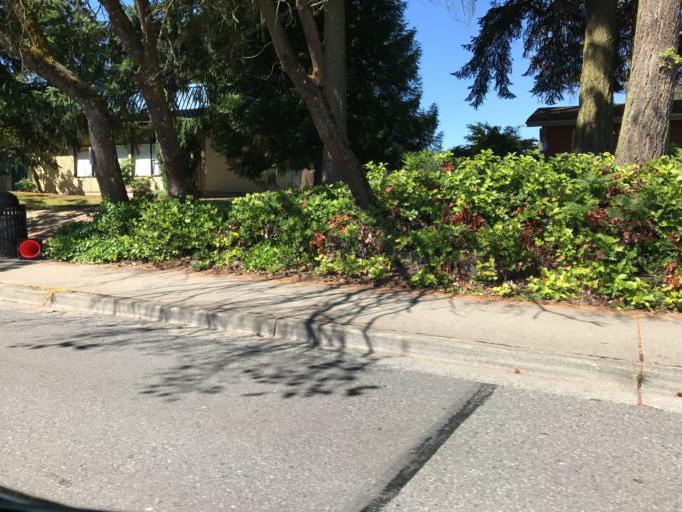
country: US
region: Washington
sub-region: King County
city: Sammamish
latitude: 47.6311
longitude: -122.1217
